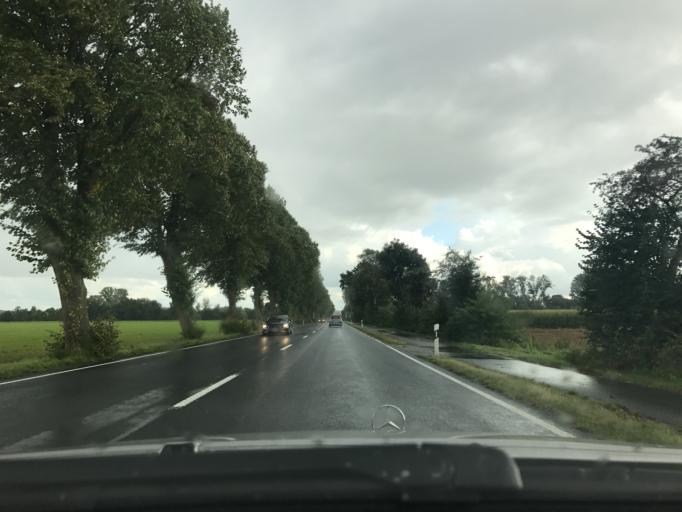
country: DE
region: North Rhine-Westphalia
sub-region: Regierungsbezirk Arnsberg
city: Soest
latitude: 51.6129
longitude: 8.1056
